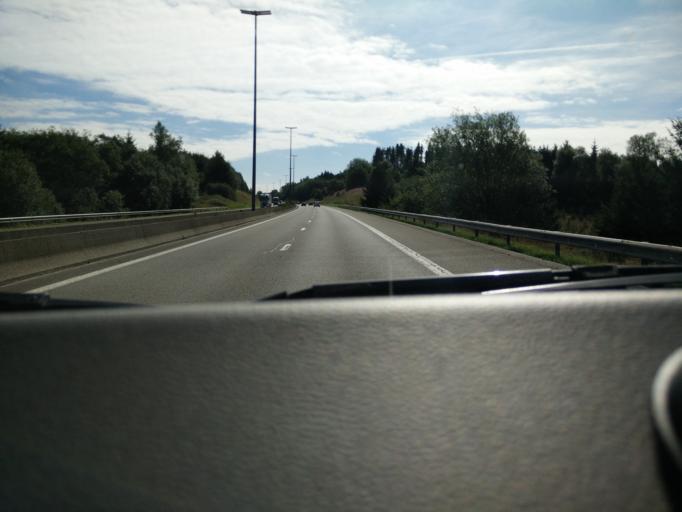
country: BE
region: Wallonia
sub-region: Province du Luxembourg
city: Bertrix
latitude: 49.9152
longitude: 5.2547
